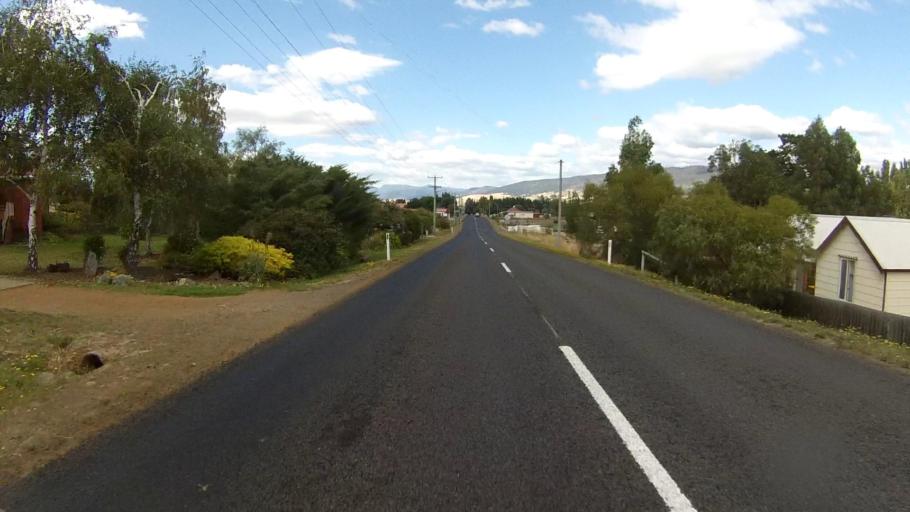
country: AU
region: Tasmania
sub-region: Derwent Valley
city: New Norfolk
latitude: -42.6944
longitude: 146.8870
